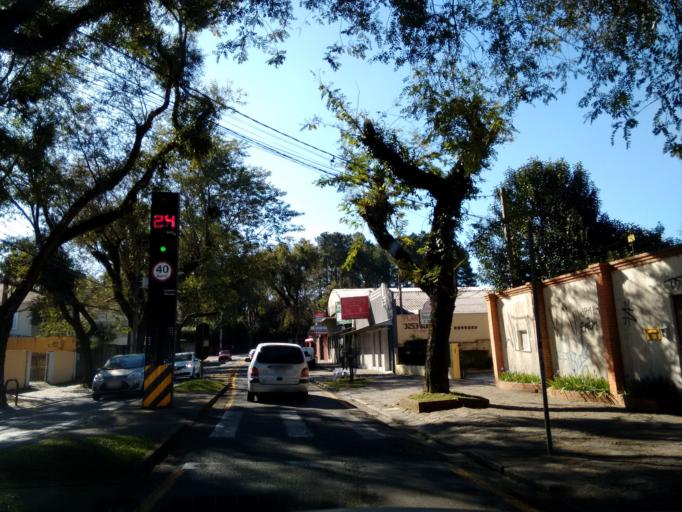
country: BR
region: Parana
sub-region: Curitiba
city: Curitiba
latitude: -25.3984
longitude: -49.2715
